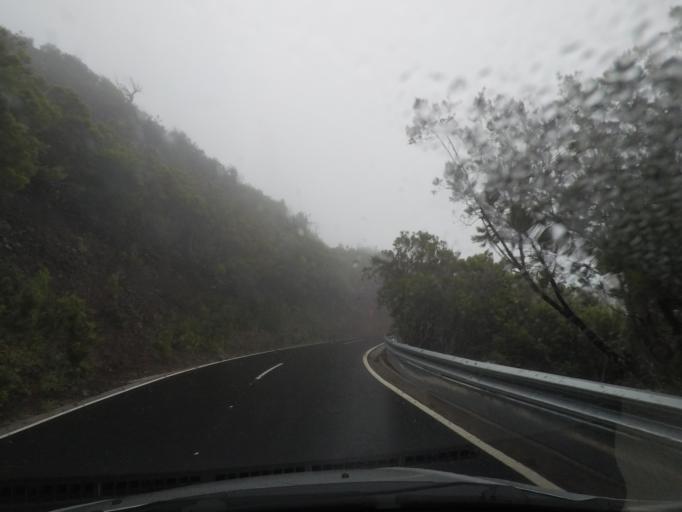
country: PT
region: Madeira
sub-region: Santana
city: Santana
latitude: 32.7689
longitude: -16.9189
